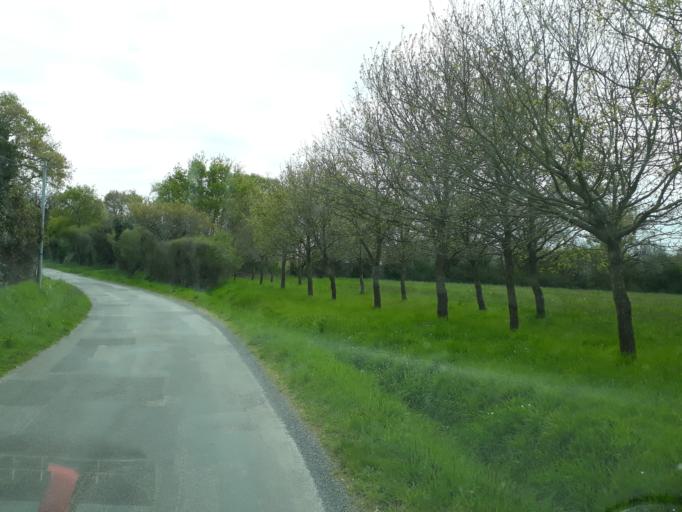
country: FR
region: Brittany
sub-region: Departement du Morbihan
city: Theix
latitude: 47.6009
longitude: -2.6845
